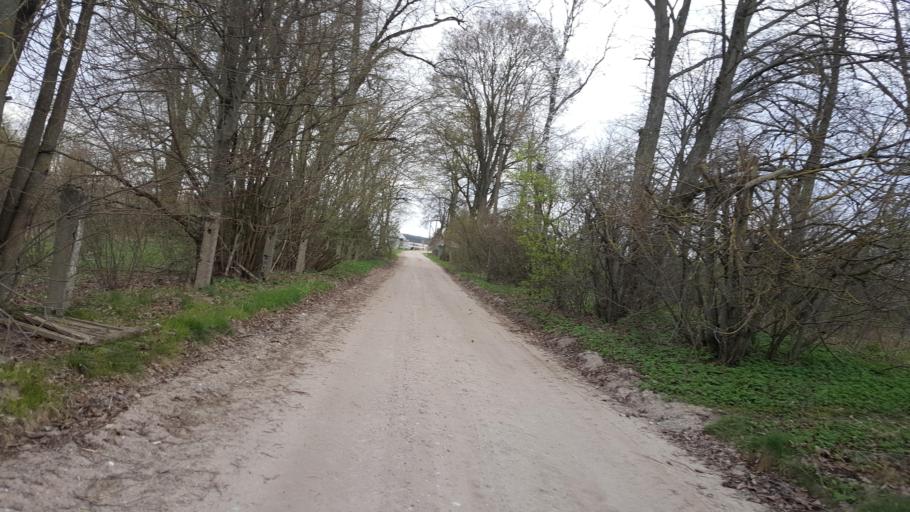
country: BY
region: Brest
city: Kamyanyets
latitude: 52.4065
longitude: 23.7140
